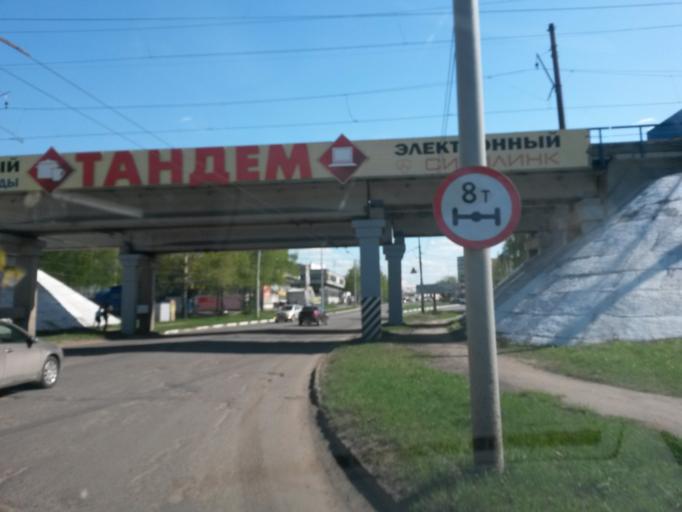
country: RU
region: Jaroslavl
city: Yaroslavl
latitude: 57.6459
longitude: 39.8806
